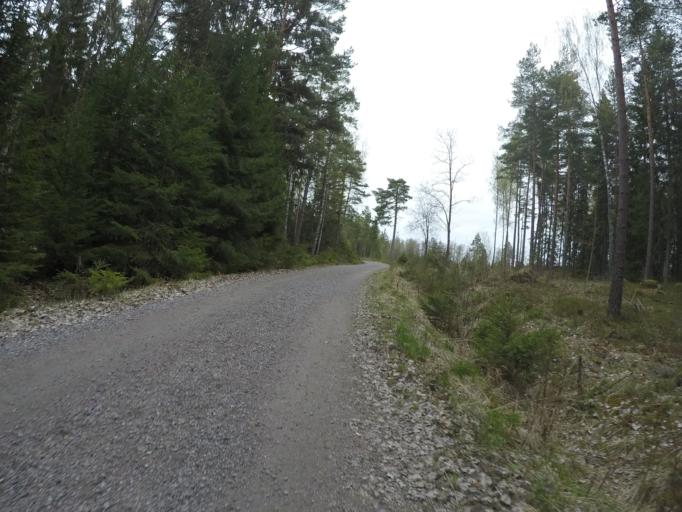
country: SE
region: Soedermanland
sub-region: Eskilstuna Kommun
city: Kvicksund
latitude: 59.4020
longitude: 16.2757
